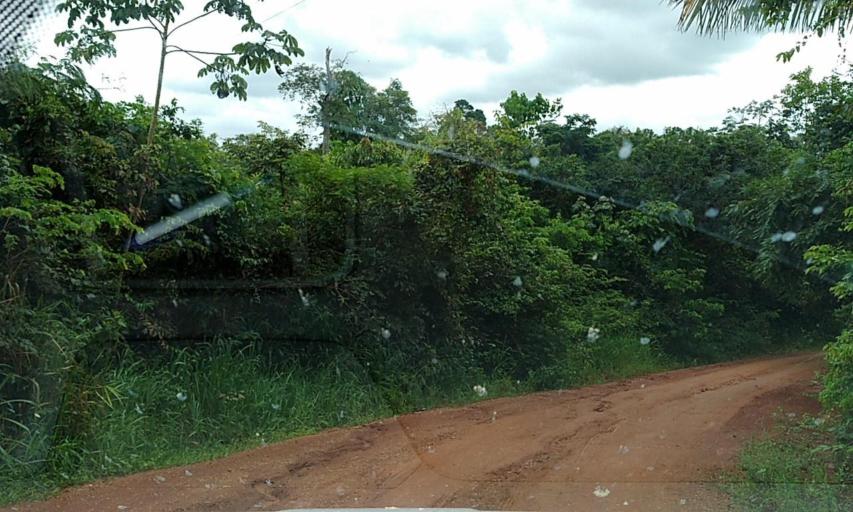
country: BR
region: Para
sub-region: Altamira
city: Altamira
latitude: -3.3067
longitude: -52.6876
